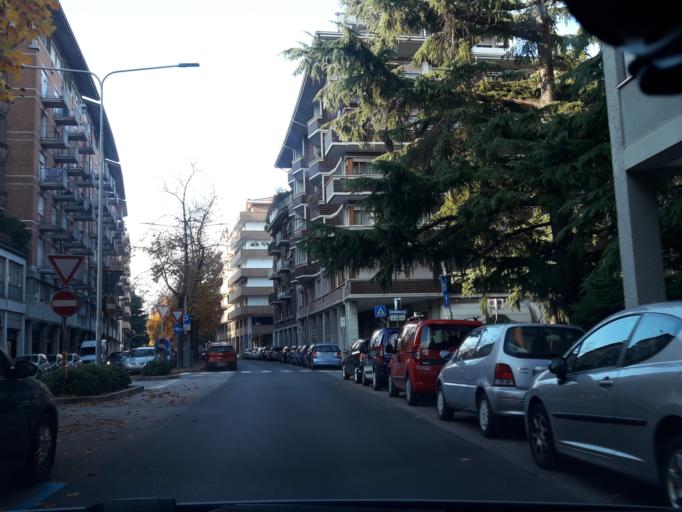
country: IT
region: Friuli Venezia Giulia
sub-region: Provincia di Udine
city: Udine
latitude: 46.0589
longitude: 13.2450
